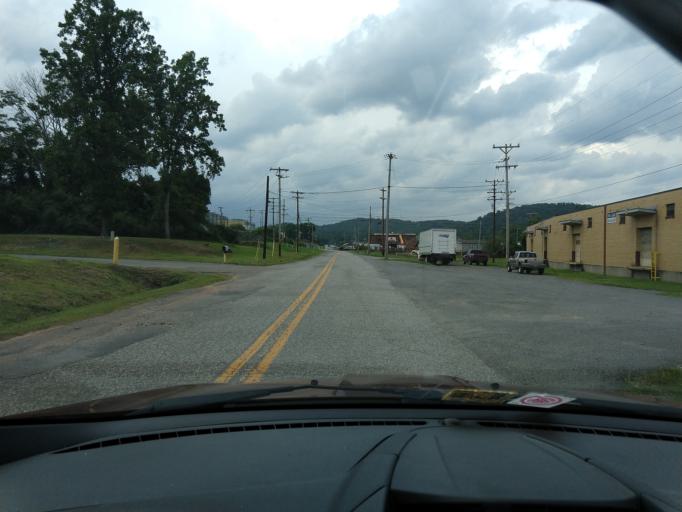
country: US
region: West Virginia
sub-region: Harrison County
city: Clarksburg
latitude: 39.2646
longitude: -80.3632
